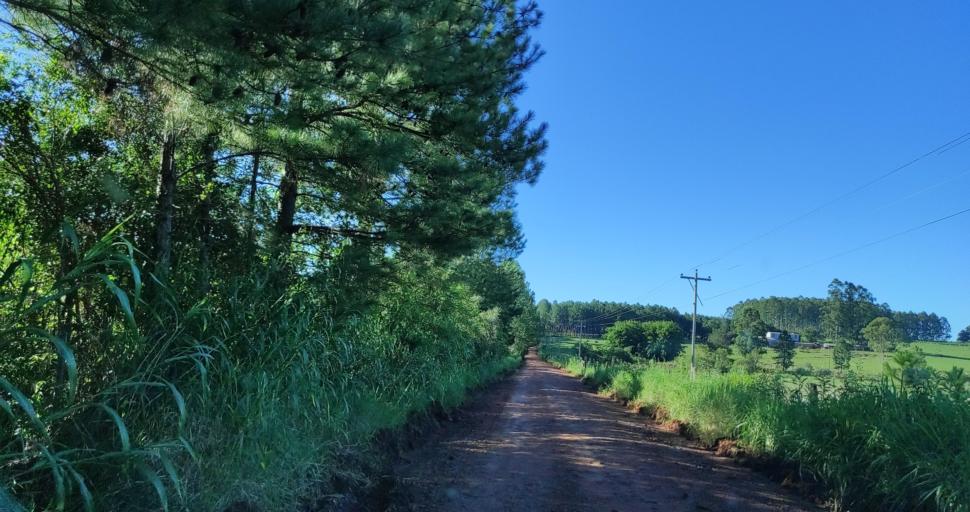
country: AR
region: Misiones
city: Puerto Rico
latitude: -26.8372
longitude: -55.0021
